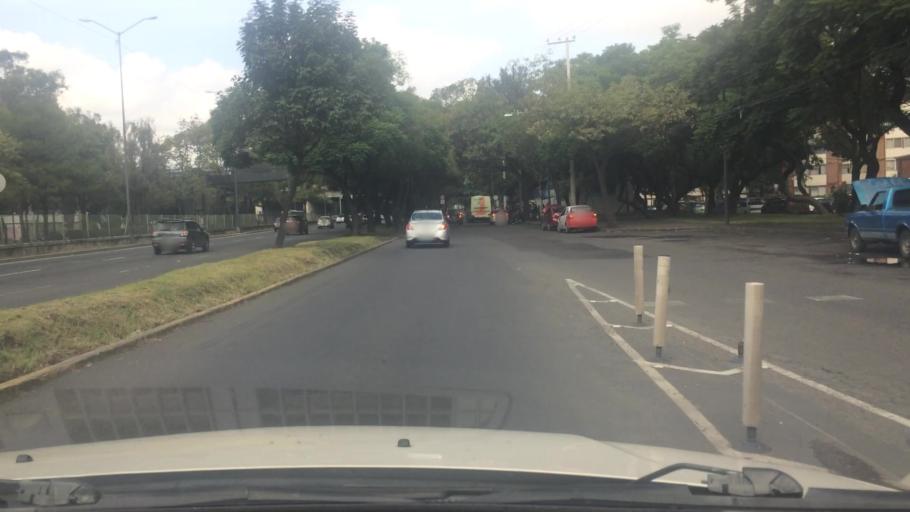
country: MX
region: Mexico City
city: Xochimilco
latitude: 19.2861
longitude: -99.1230
